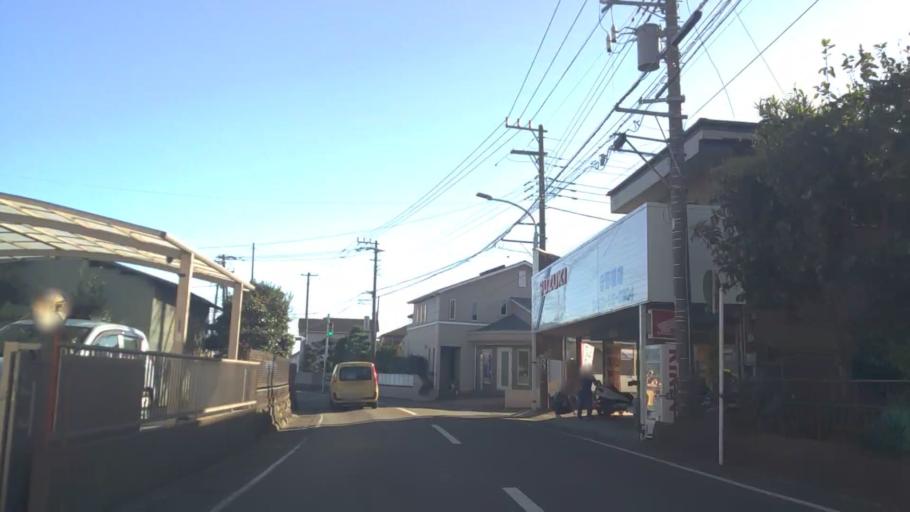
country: JP
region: Kanagawa
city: Atsugi
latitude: 35.3862
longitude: 139.3664
